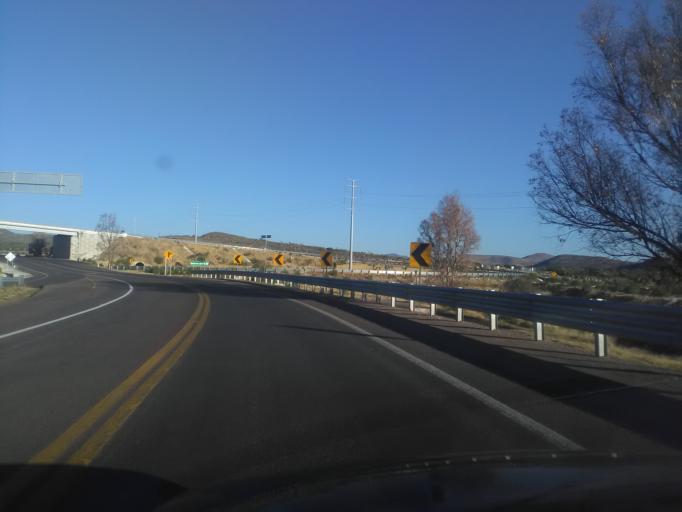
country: MX
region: Durango
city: Victoria de Durango
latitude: 23.9968
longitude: -104.7229
